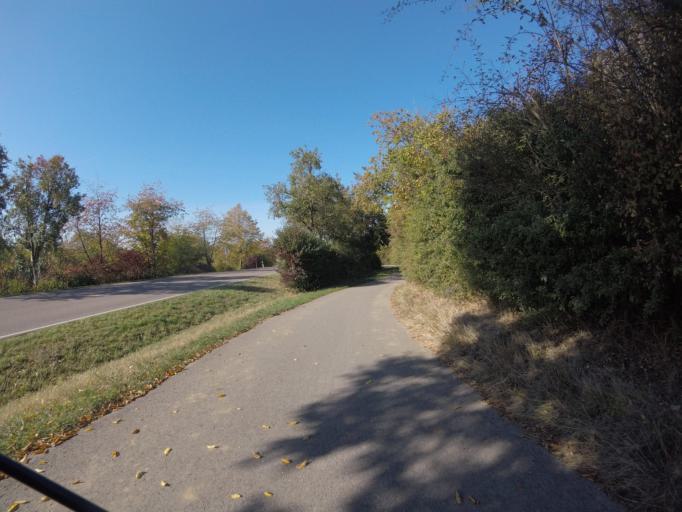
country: DE
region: Baden-Wuerttemberg
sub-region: Regierungsbezirk Stuttgart
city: Sersheim
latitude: 48.9643
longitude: 9.0251
